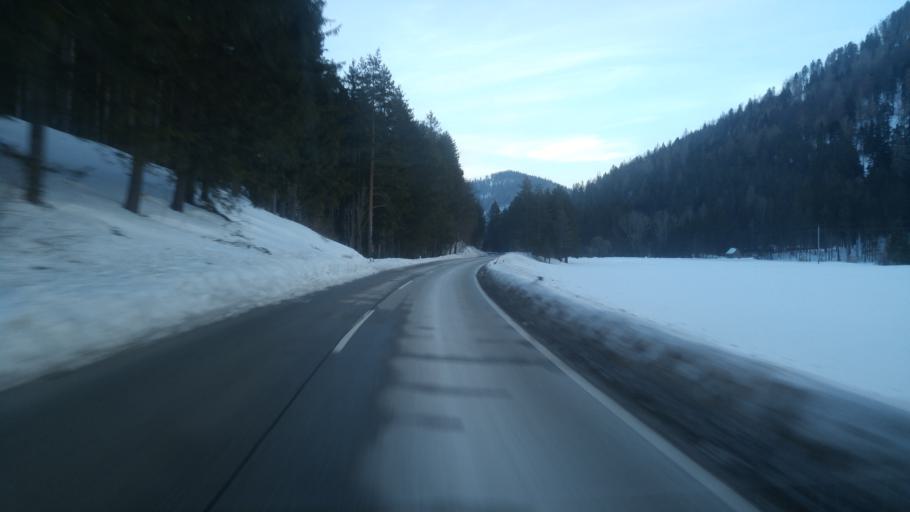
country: AT
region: Lower Austria
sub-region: Politischer Bezirk Wiener Neustadt
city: Rohr im Gebirge
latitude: 47.8860
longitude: 15.7525
